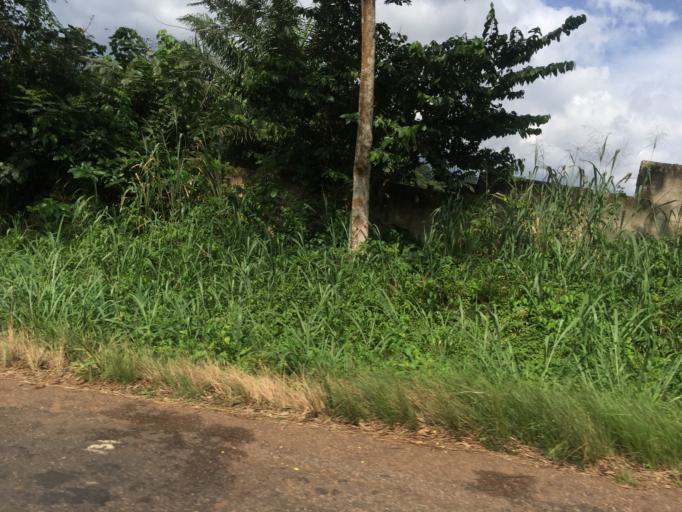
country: GH
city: Mpraeso
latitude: 6.6048
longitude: -0.7395
